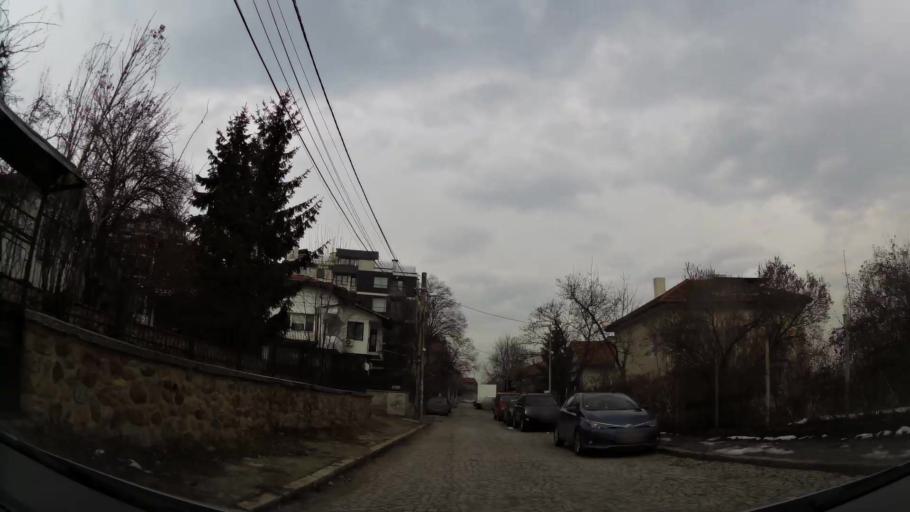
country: BG
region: Sofia-Capital
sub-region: Stolichna Obshtina
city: Sofia
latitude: 42.6631
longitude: 23.2425
